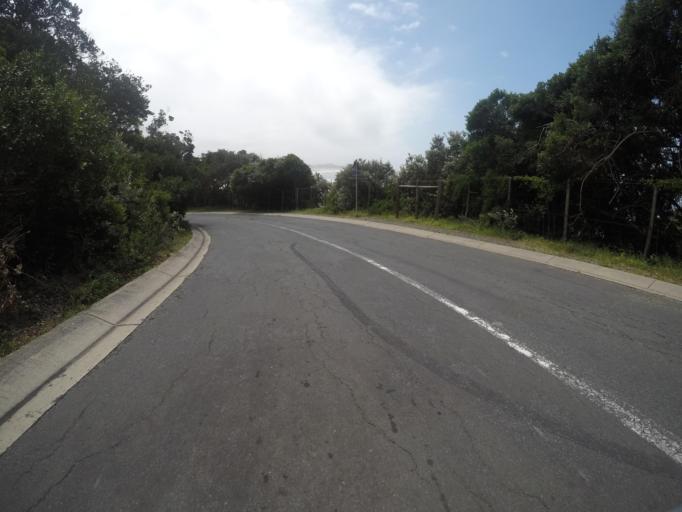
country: ZA
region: Eastern Cape
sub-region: Buffalo City Metropolitan Municipality
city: East London
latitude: -32.9944
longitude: 27.9485
